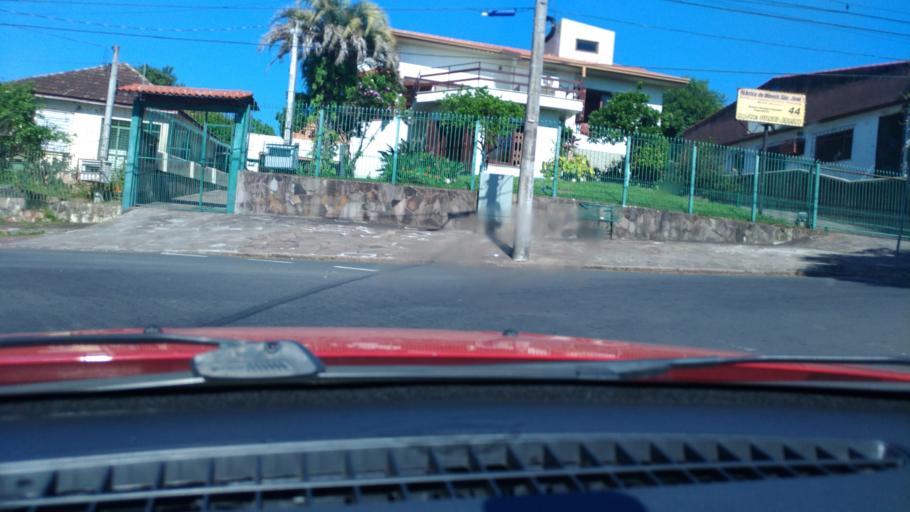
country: BR
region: Rio Grande do Sul
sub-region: Porto Alegre
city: Porto Alegre
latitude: -30.0300
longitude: -51.1475
